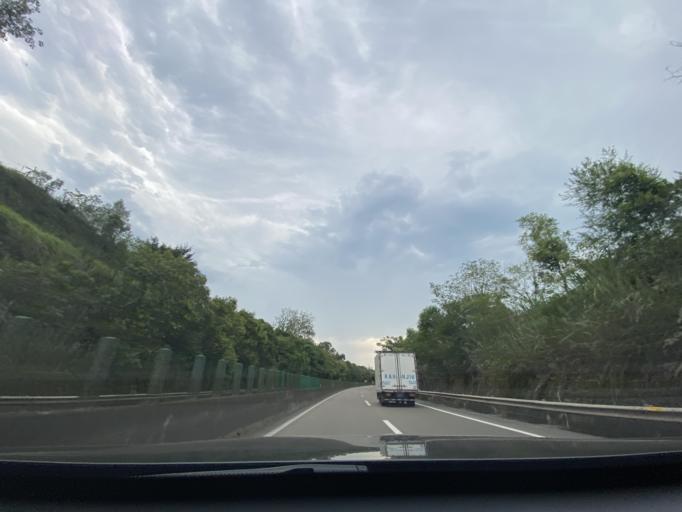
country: CN
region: Sichuan
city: Chonglong
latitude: 29.7240
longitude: 104.9244
